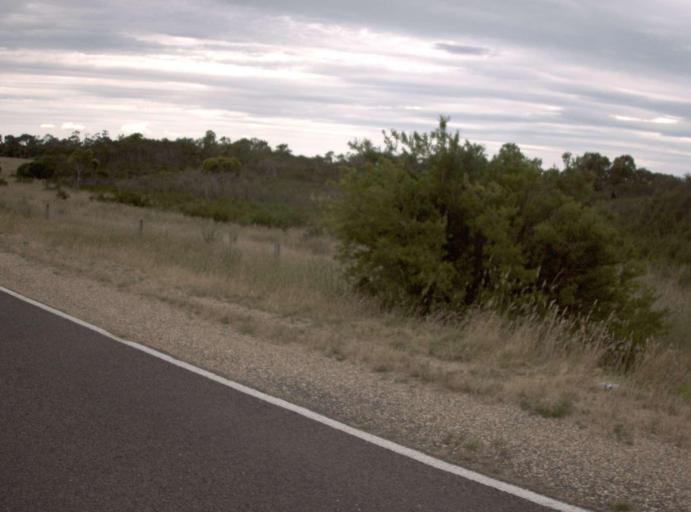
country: AU
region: Victoria
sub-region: East Gippsland
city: Bairnsdale
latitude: -38.0012
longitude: 147.3969
